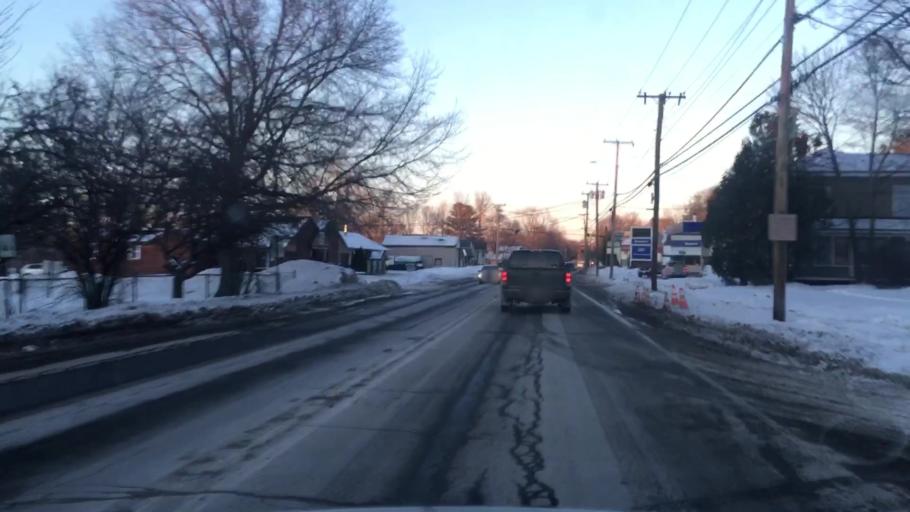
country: US
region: Maine
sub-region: Penobscot County
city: Bangor
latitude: 44.7772
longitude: -68.7778
